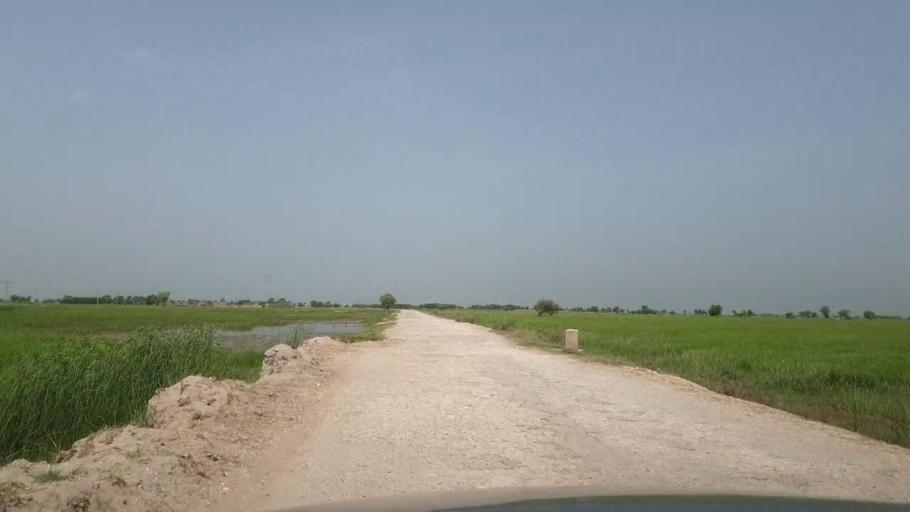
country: PK
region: Sindh
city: Garhi Yasin
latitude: 27.8596
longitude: 68.4078
